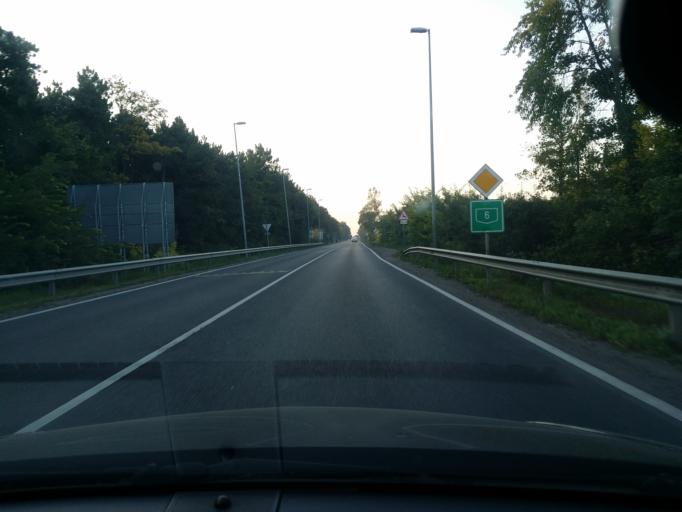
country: HU
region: Fejer
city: dunaujvaros
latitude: 46.9593
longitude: 18.9099
